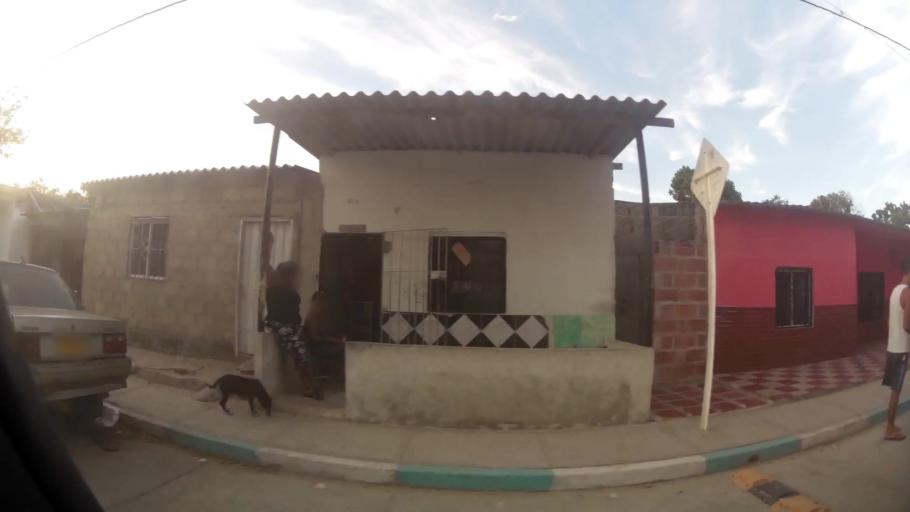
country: CO
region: Atlantico
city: Barranquilla
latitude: 10.9536
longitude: -74.8290
